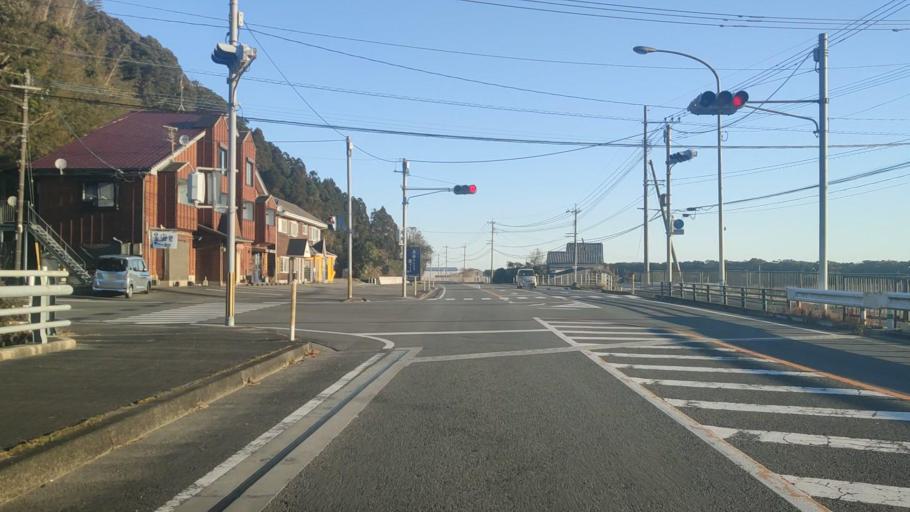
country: JP
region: Miyazaki
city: Takanabe
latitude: 32.0956
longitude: 131.5172
